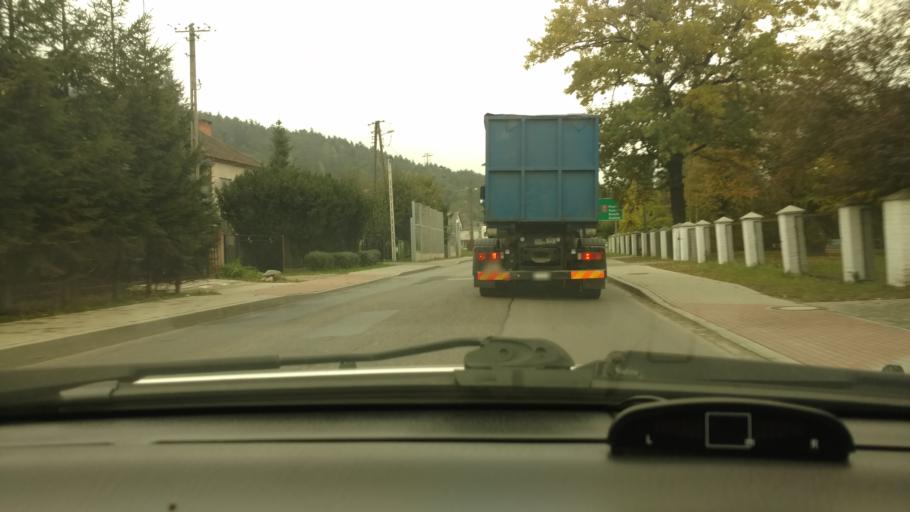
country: PL
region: Lesser Poland Voivodeship
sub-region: Powiat nowosadecki
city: Chelmiec
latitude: 49.6388
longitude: 20.6657
